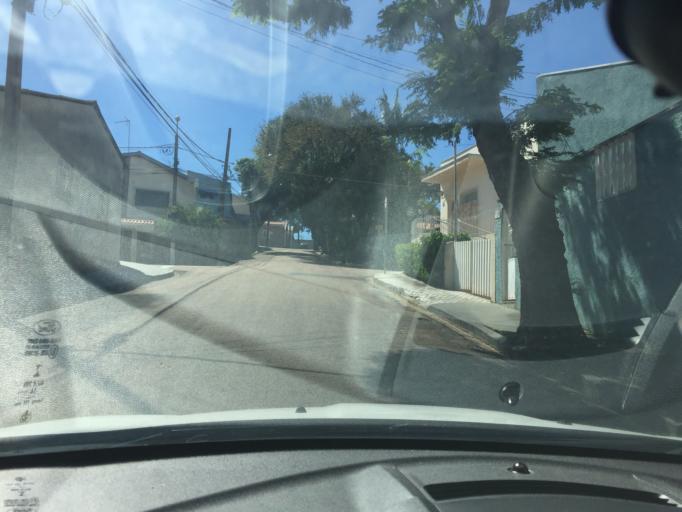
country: BR
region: Sao Paulo
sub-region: Jundiai
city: Jundiai
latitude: -23.1798
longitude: -46.8952
